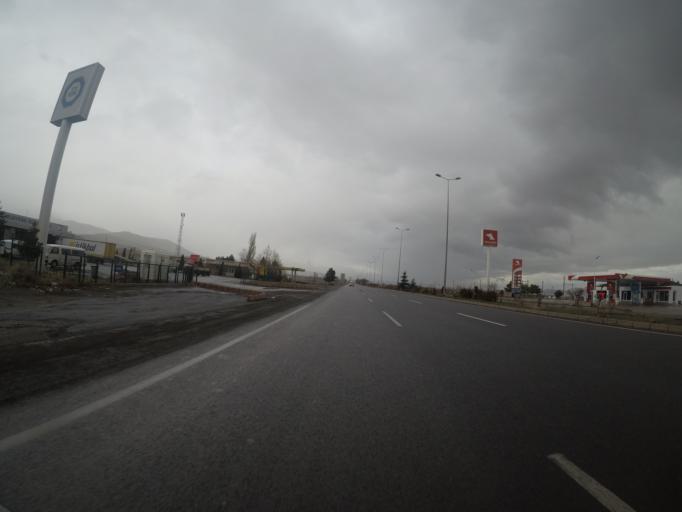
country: TR
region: Kayseri
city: Incesu
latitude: 38.6844
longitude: 35.2374
